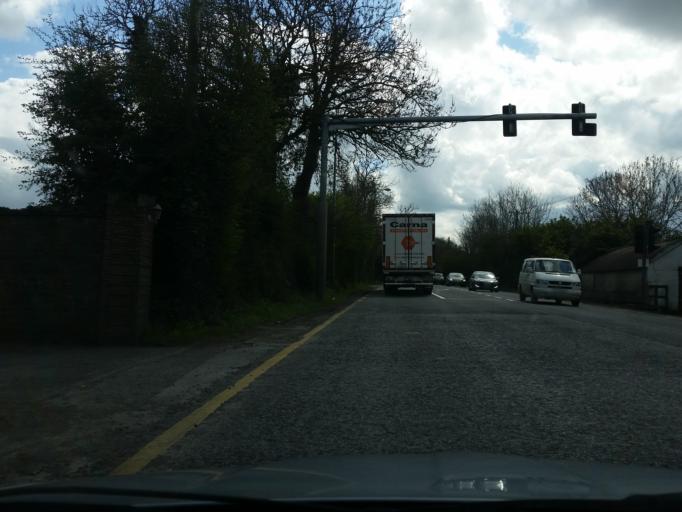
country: IE
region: Leinster
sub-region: An Mhi
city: Ratoath
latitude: 53.5585
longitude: -6.4402
